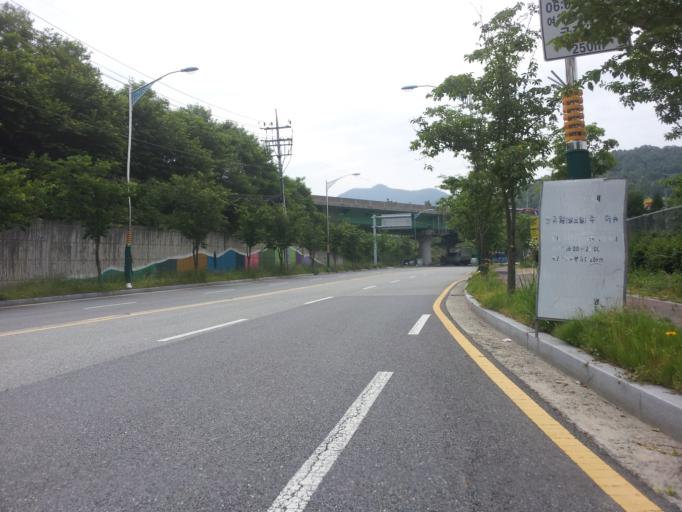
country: KR
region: Daejeon
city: Daejeon
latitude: 36.3330
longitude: 127.4795
